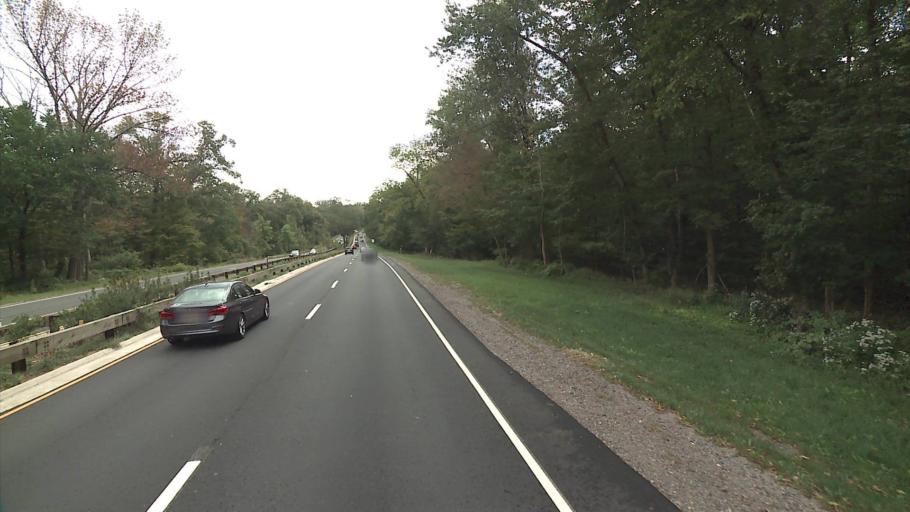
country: US
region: Connecticut
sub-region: Fairfield County
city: North Stamford
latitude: 41.1165
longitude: -73.5342
